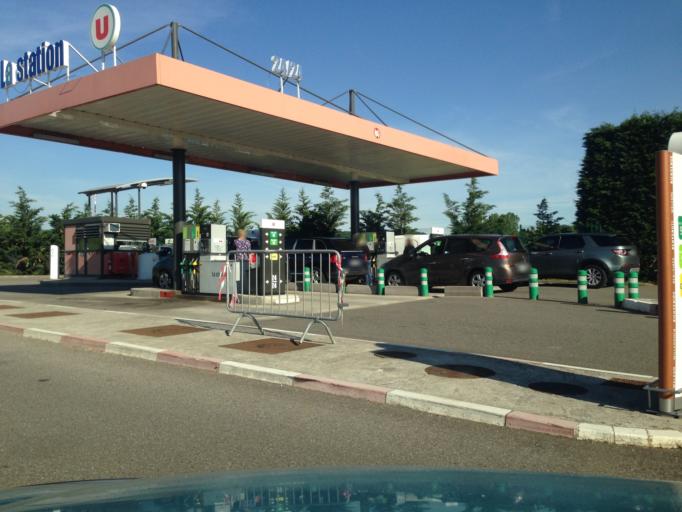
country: FR
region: Alsace
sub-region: Departement du Bas-Rhin
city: Ingwiller
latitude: 48.8682
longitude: 7.4700
